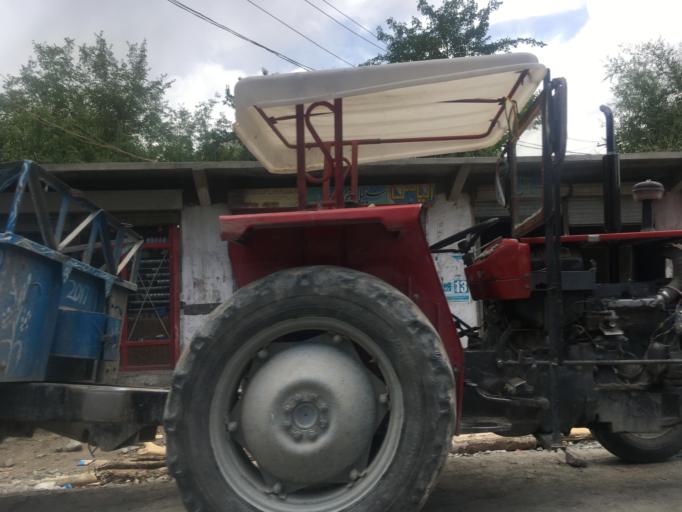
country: PK
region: Gilgit-Baltistan
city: Skardu
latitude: 35.2943
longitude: 75.6111
